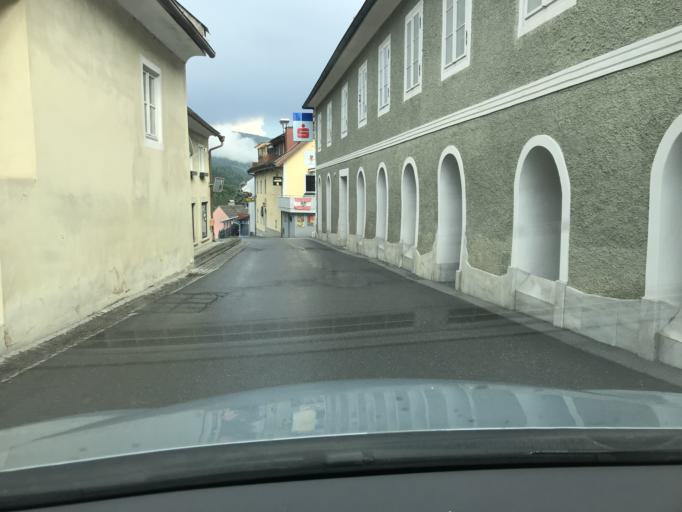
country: AT
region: Styria
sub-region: Politischer Bezirk Murau
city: Sankt Peter am Kammersberg
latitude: 47.1872
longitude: 14.1872
